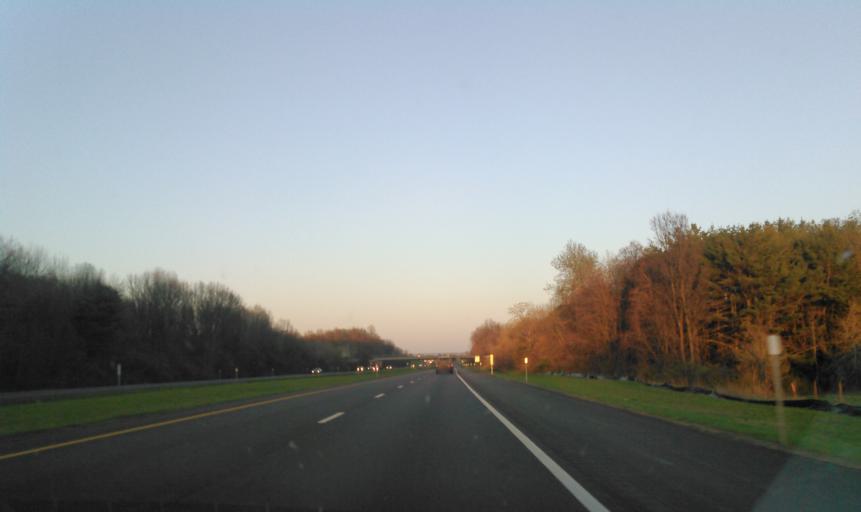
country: US
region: New York
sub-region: Seneca County
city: Waterloo
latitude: 42.9596
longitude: -76.9426
